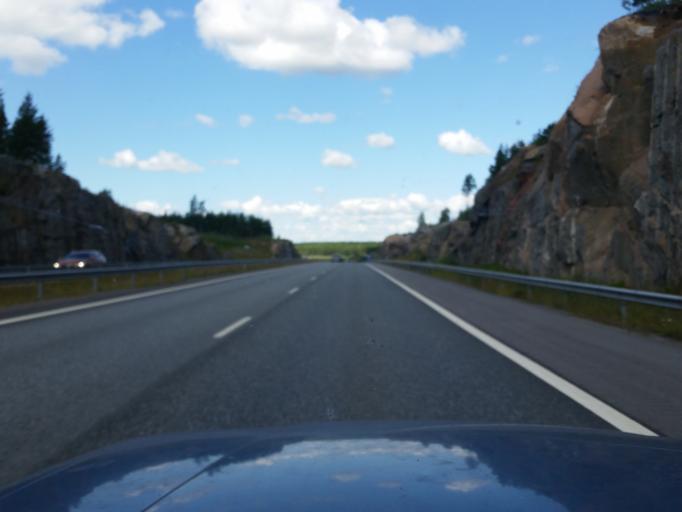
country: FI
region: Varsinais-Suomi
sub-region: Salo
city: Suomusjaervi
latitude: 60.3746
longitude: 23.6422
